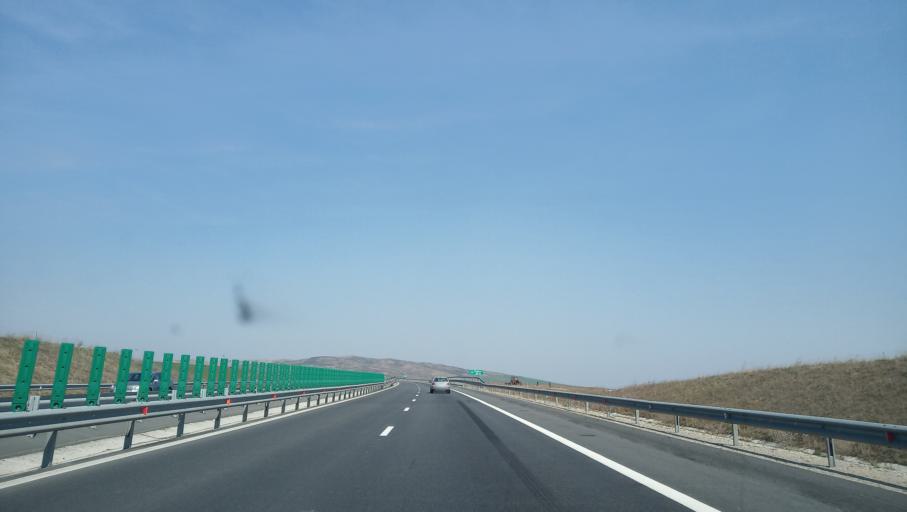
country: RO
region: Alba
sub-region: Comuna Unirea
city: Unirea
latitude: 46.3967
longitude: 23.7915
